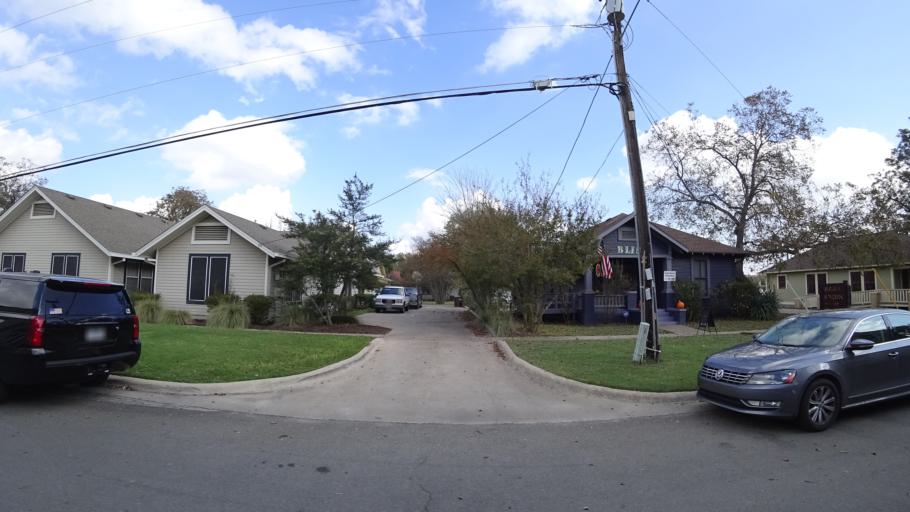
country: US
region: Texas
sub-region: Williamson County
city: Round Rock
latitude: 30.5087
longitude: -97.6766
